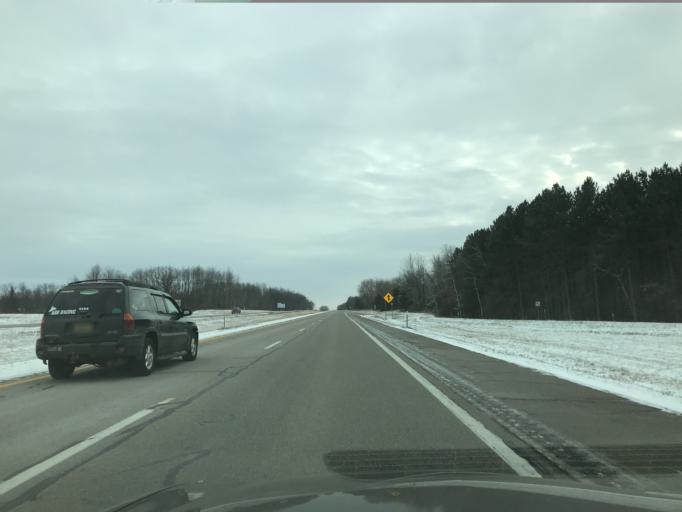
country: US
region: Michigan
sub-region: Roscommon County
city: Houghton Lake
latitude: 44.3342
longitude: -84.8071
